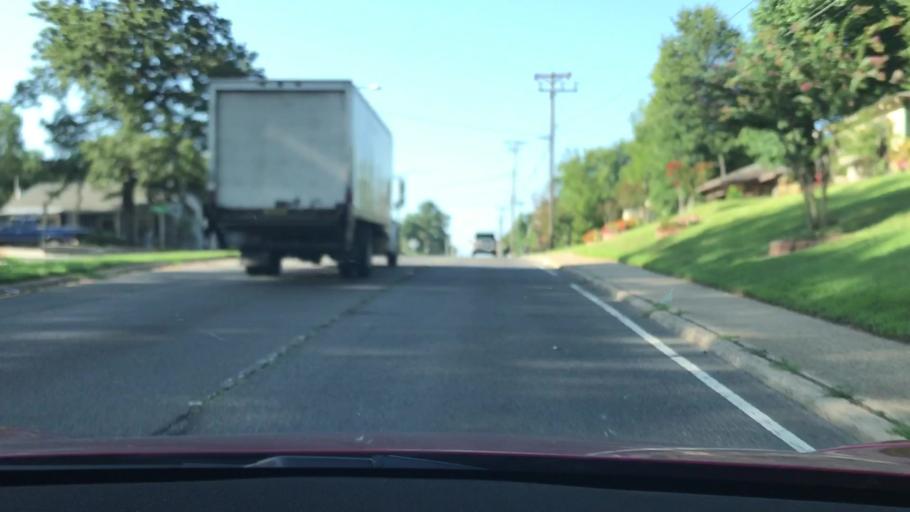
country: US
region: Louisiana
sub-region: Caddo Parish
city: Shreveport
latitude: 32.4686
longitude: -93.7801
